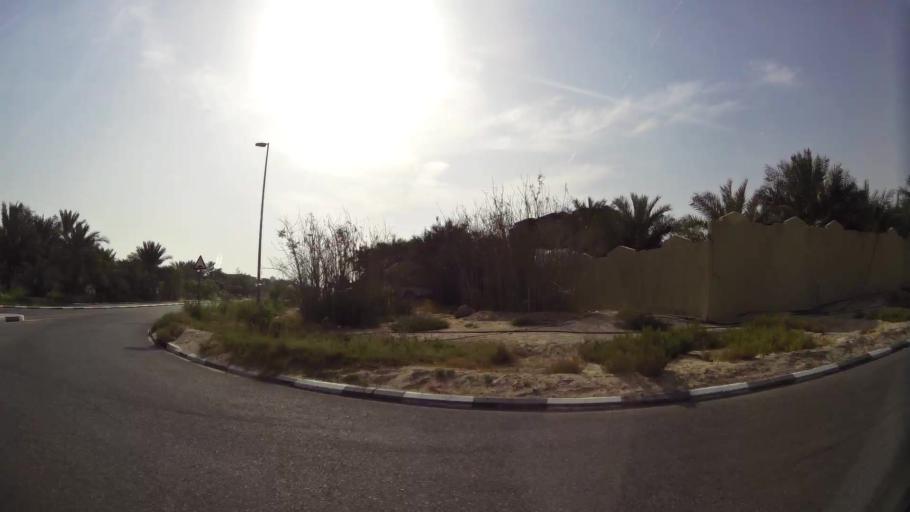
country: AE
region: Ash Shariqah
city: Sharjah
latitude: 25.2432
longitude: 55.4067
